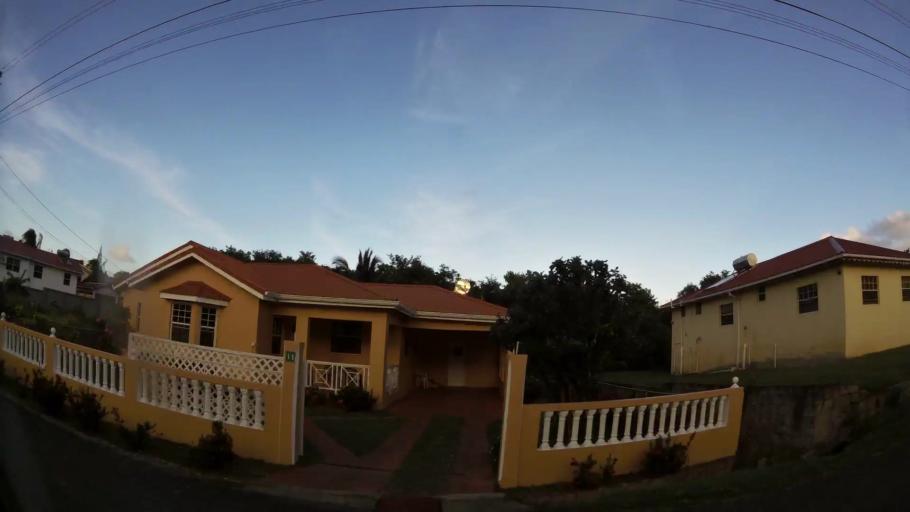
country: LC
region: Gros-Islet
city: Gros Islet
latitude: 14.0736
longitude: -60.9380
